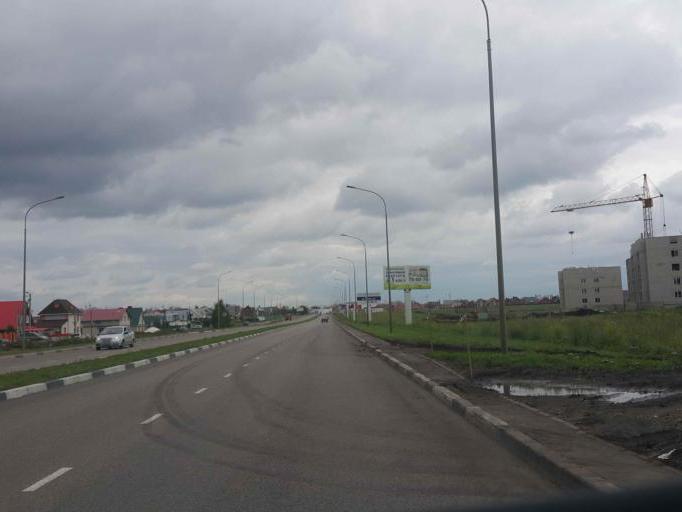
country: RU
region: Tambov
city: Komsomolets
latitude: 52.7858
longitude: 41.3697
